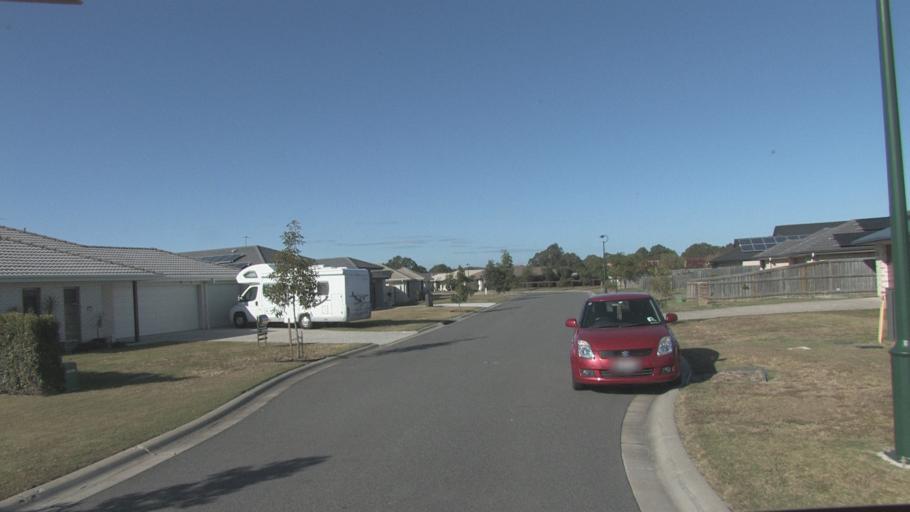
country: AU
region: Queensland
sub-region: Logan
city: Waterford West
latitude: -27.6860
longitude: 153.1719
